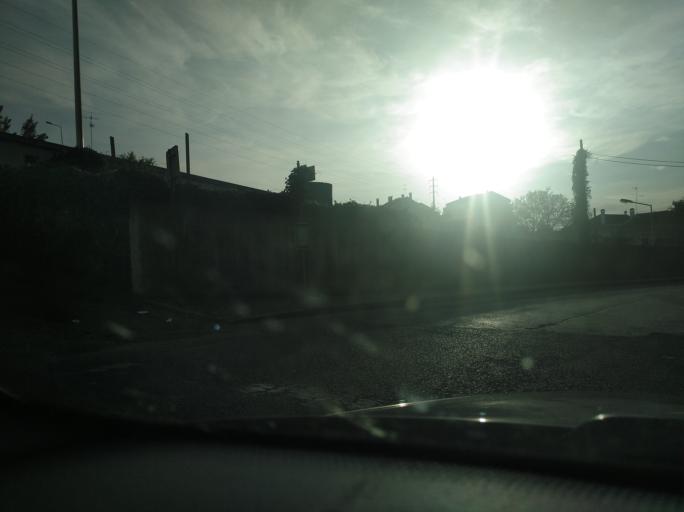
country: PT
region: Lisbon
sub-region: Odivelas
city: Odivelas
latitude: 38.7756
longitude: -9.1785
